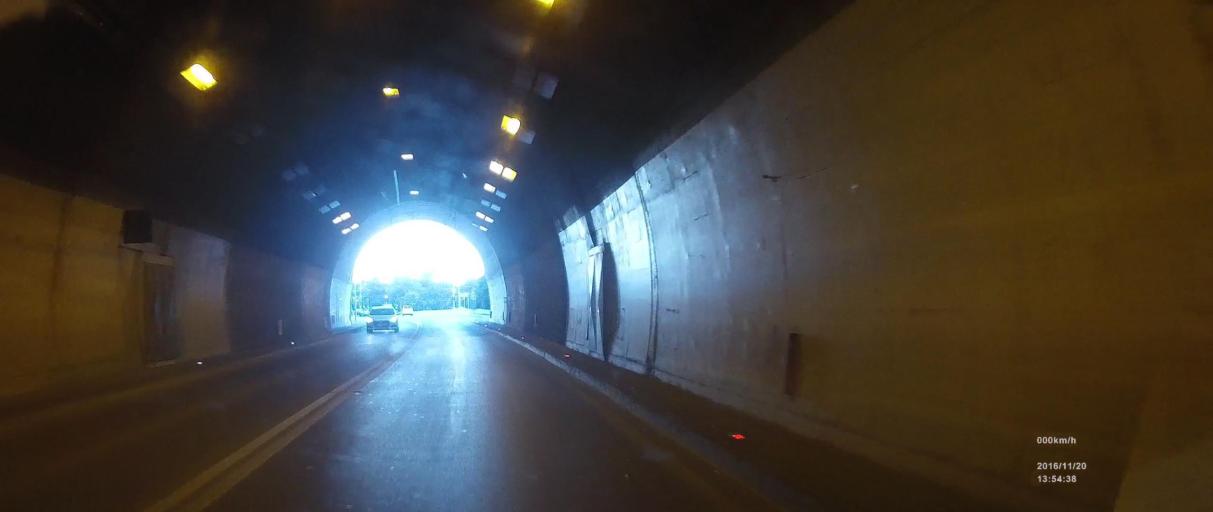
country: HR
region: Splitsko-Dalmatinska
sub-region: Grad Split
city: Split
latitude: 43.5064
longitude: 16.4241
